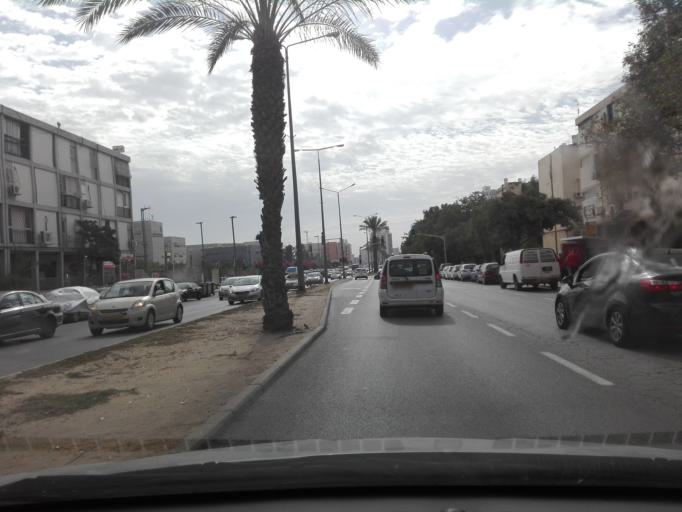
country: IL
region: Southern District
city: Beersheba
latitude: 31.2646
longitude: 34.7981
